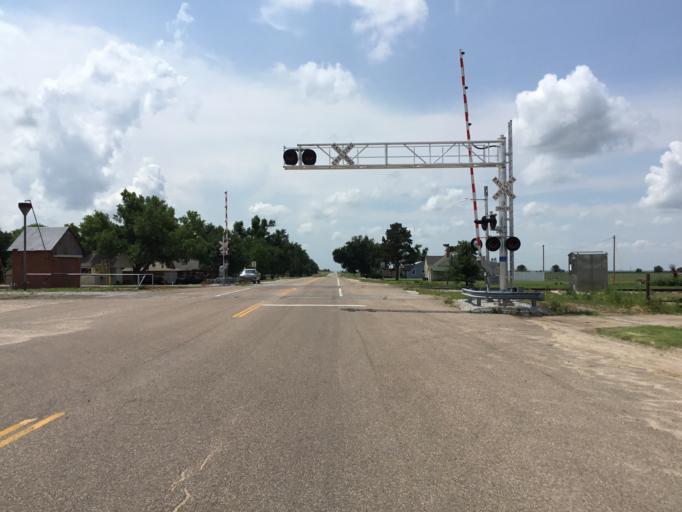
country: US
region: Kansas
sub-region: Pratt County
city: Pratt
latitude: 37.4980
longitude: -98.6839
